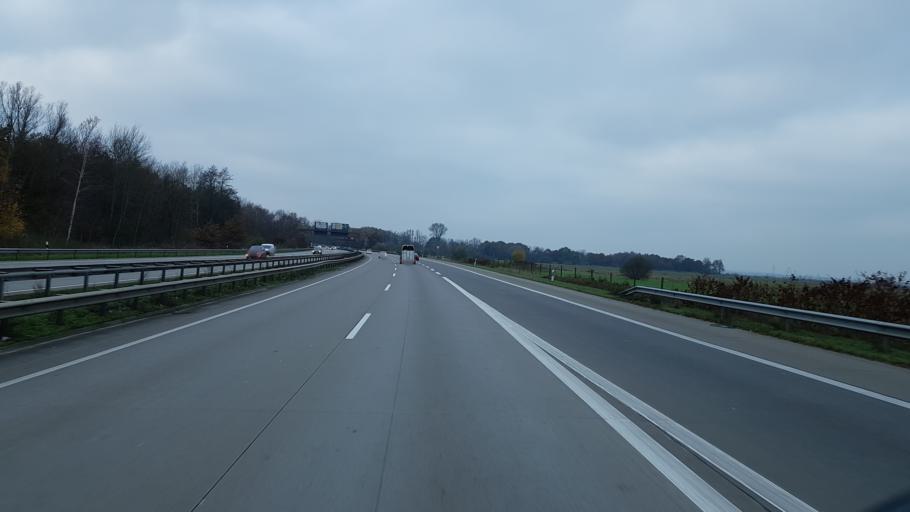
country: DE
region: Lower Saxony
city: Lilienthal
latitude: 53.1130
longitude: 8.8609
